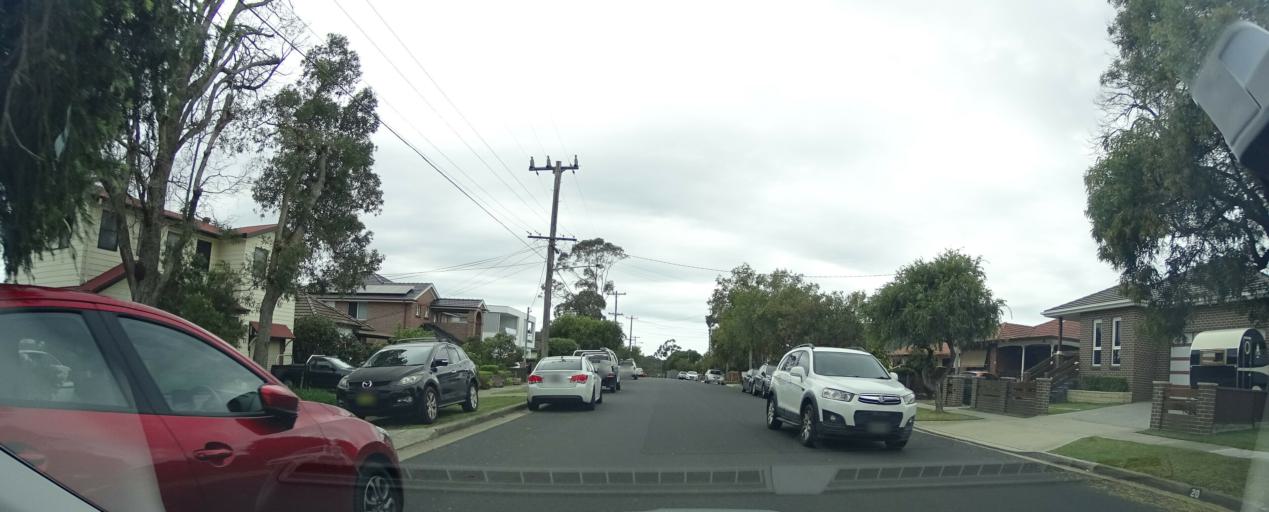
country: AU
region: New South Wales
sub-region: Bankstown
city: Revesby
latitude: -33.9682
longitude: 151.0103
